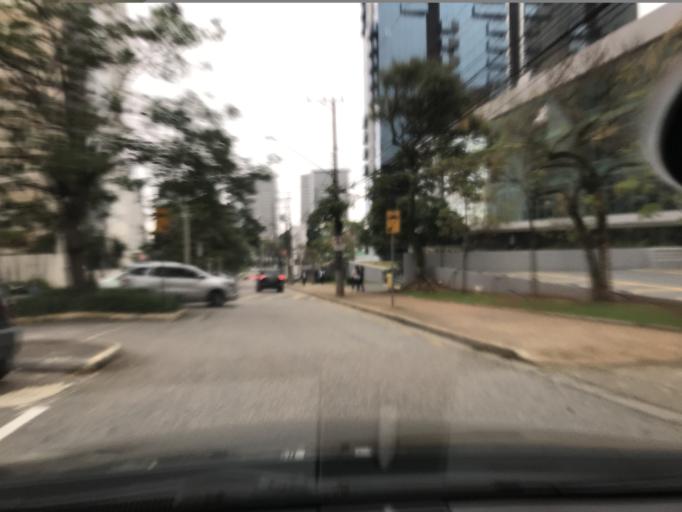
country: BR
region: Sao Paulo
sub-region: Carapicuiba
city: Carapicuiba
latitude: -23.4963
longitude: -46.8469
